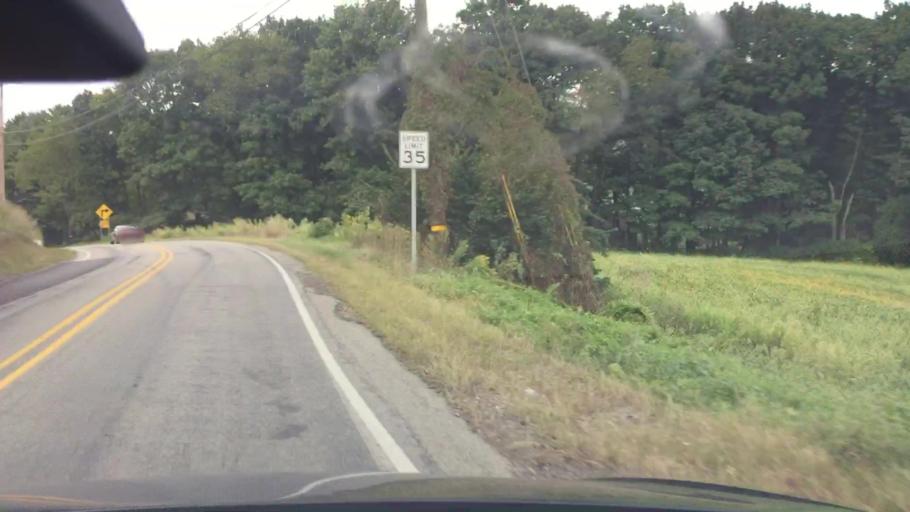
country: US
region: Pennsylvania
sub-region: Butler County
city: Meadowood
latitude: 40.8368
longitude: -79.8771
